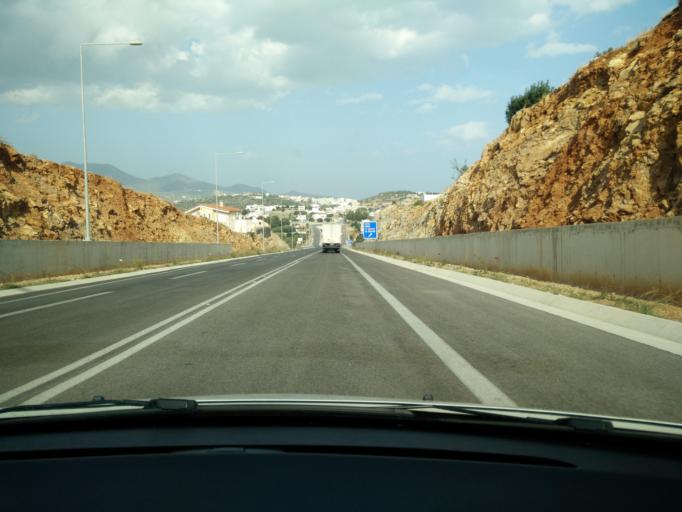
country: GR
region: Crete
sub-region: Nomos Lasithiou
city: Agios Nikolaos
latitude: 35.1802
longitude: 25.7022
